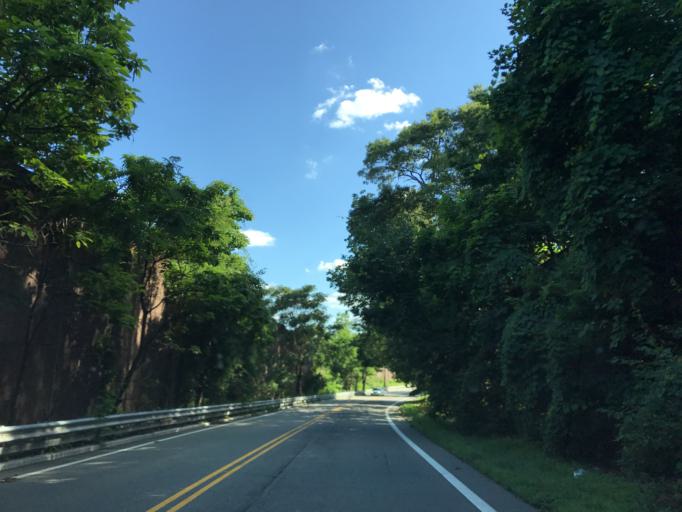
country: US
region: New Jersey
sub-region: Morris County
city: Boonton
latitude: 40.8899
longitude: -74.4159
